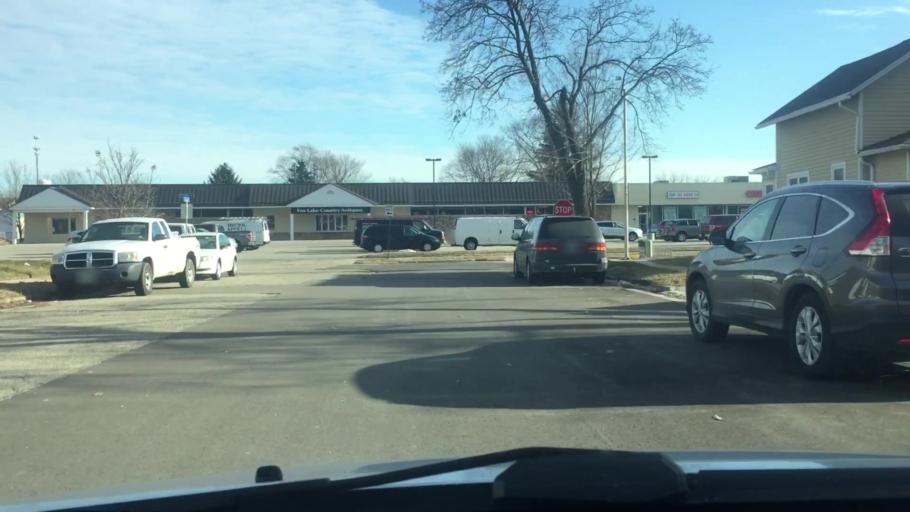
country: US
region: Wisconsin
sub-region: Waukesha County
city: Oconomowoc
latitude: 43.1101
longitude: -88.4933
